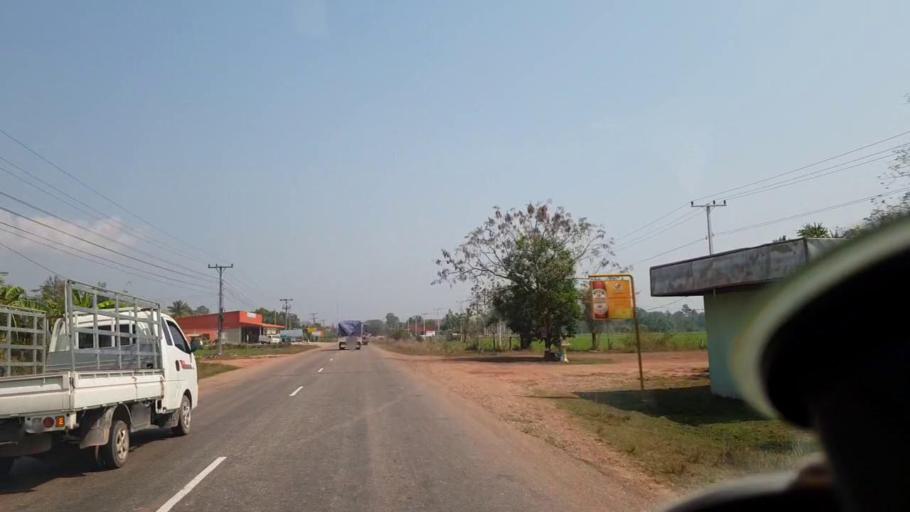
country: TH
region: Nong Khai
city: Phon Phisai
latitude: 18.1171
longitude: 103.0292
